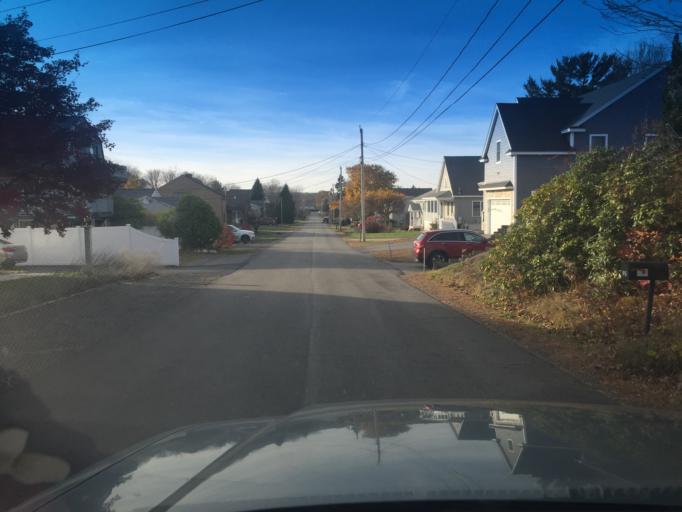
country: US
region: Maine
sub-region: York County
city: York Beach
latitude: 43.1703
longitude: -70.6014
